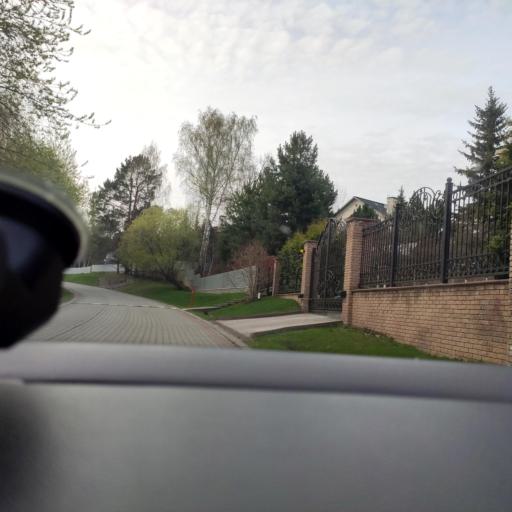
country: RU
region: Moskovskaya
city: Zhavoronki
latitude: 55.6888
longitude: 37.0957
